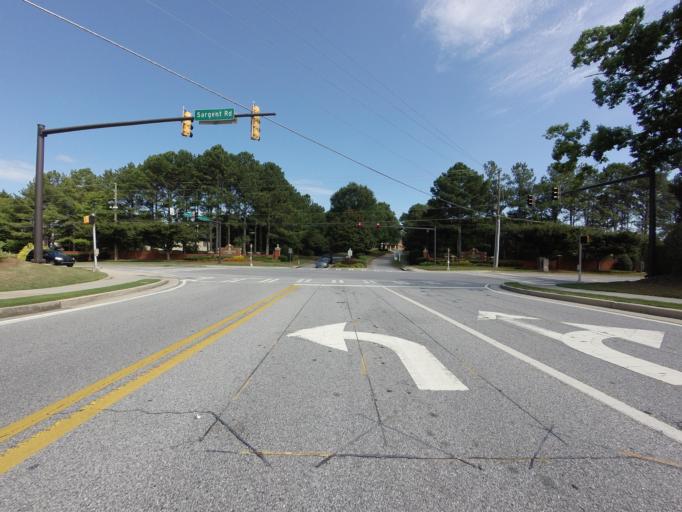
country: US
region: Georgia
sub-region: Fulton County
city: Johns Creek
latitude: 34.0692
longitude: -84.1846
